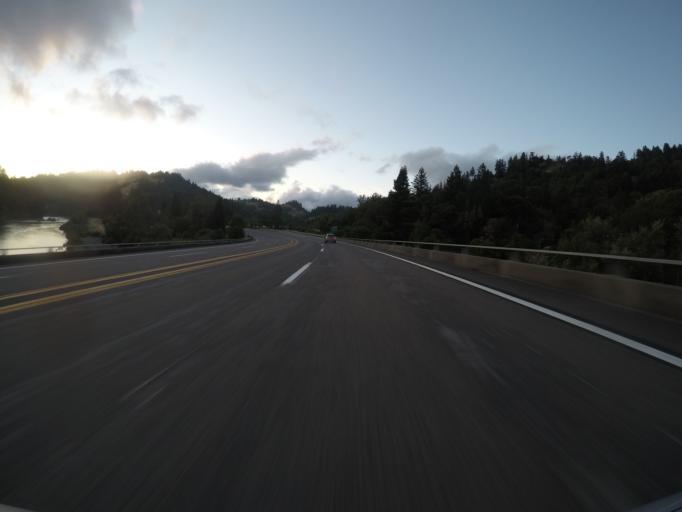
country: US
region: California
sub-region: Humboldt County
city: Redway
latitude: 40.0625
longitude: -123.7834
